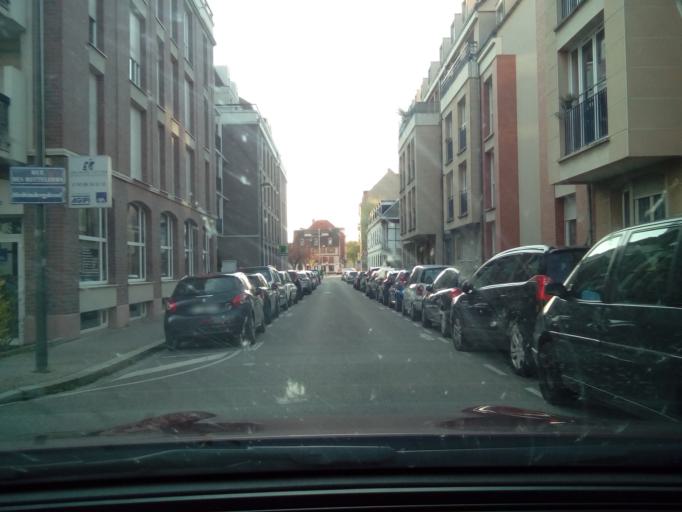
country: FR
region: Alsace
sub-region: Departement du Bas-Rhin
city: Strasbourg
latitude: 48.5776
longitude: 7.7417
